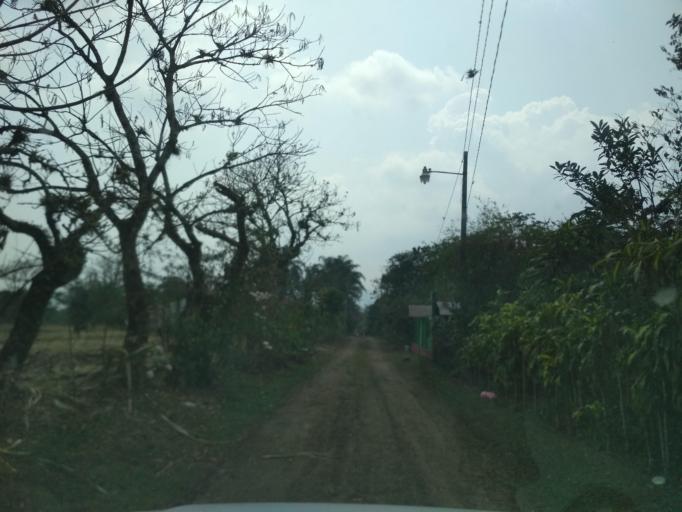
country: MX
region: Veracruz
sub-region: Cordoba
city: Fredepo
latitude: 18.8568
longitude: -96.9795
